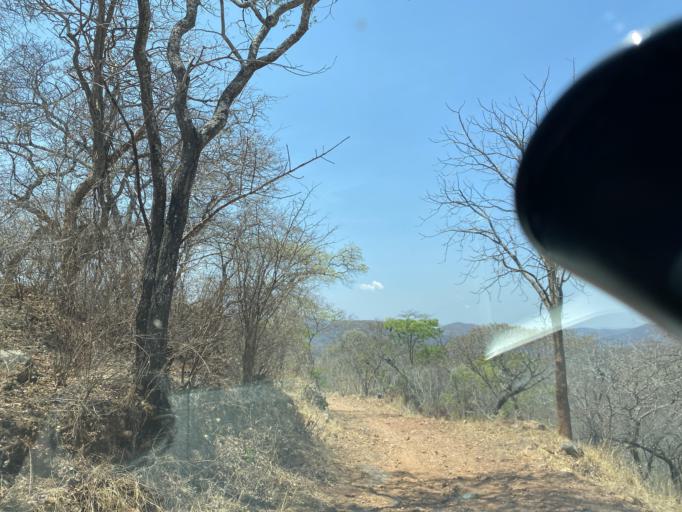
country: ZM
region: Lusaka
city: Kafue
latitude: -15.7991
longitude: 28.4566
